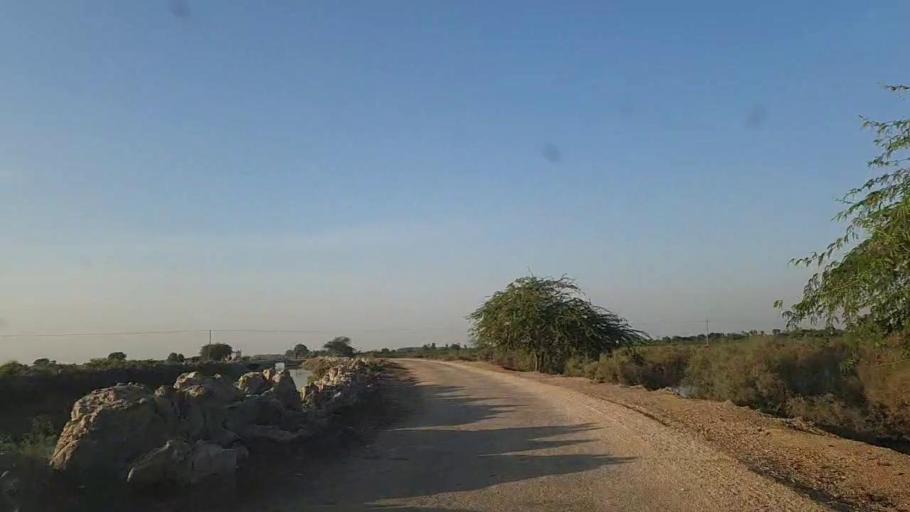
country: PK
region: Sindh
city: Mirpur Batoro
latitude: 24.6964
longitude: 68.2007
